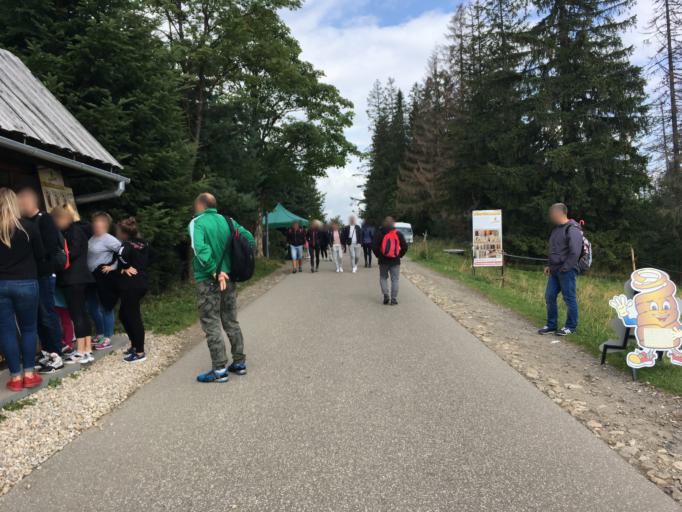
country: PL
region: Lesser Poland Voivodeship
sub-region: Powiat tatrzanski
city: Zakopane
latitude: 49.3047
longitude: 19.9251
